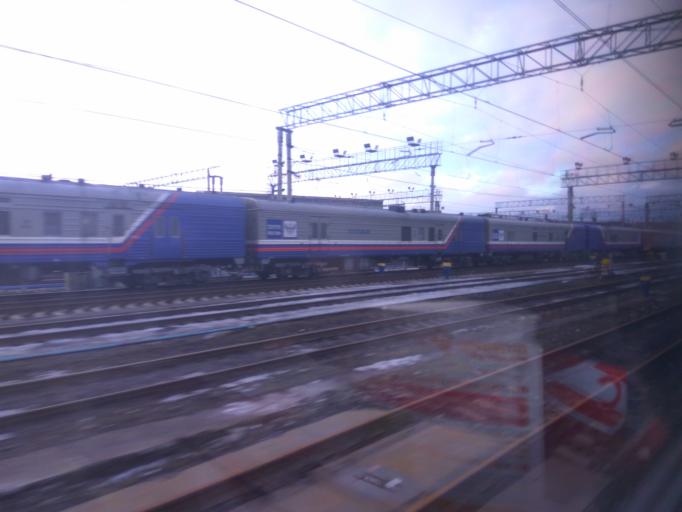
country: RU
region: St.-Petersburg
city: Centralniy
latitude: 59.9190
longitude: 30.3665
